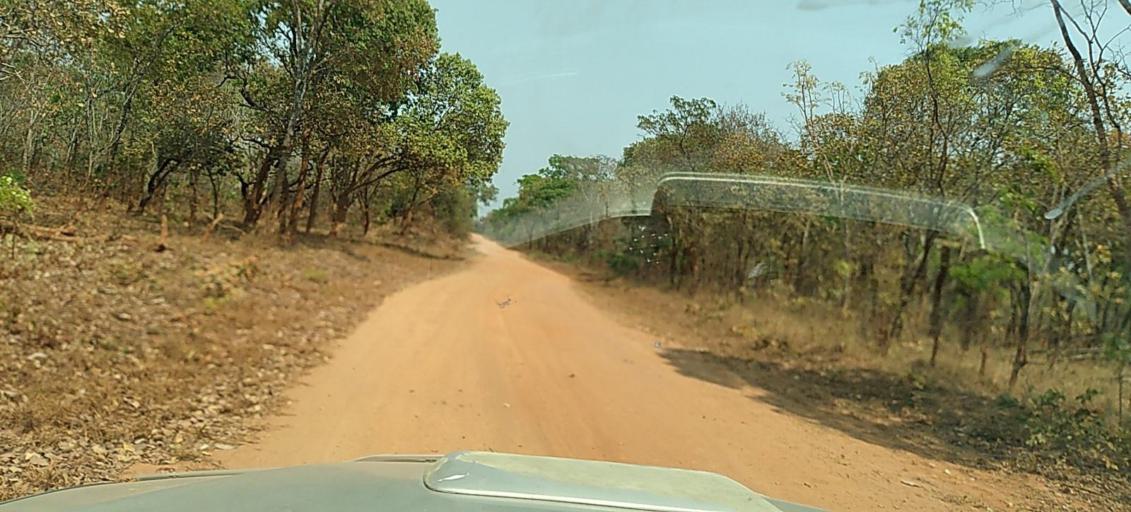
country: ZM
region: North-Western
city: Kasempa
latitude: -13.6867
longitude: 26.3205
